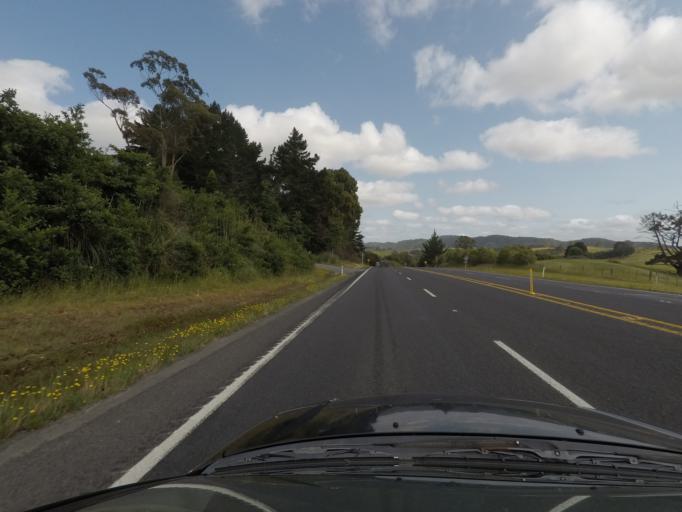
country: NZ
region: Northland
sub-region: Whangarei
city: Whangarei
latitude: -35.8083
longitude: 174.2959
